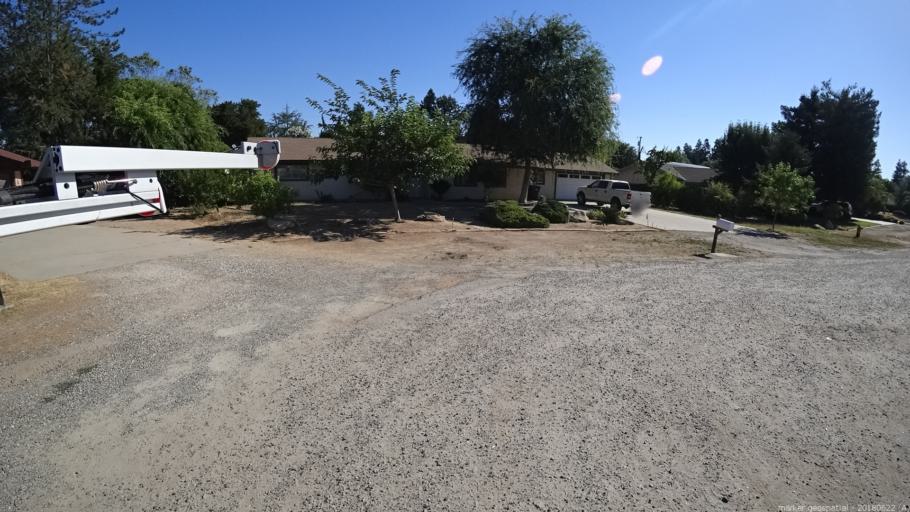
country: US
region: California
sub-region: Madera County
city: Bonadelle Ranchos-Madera Ranchos
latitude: 36.9049
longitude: -119.7998
